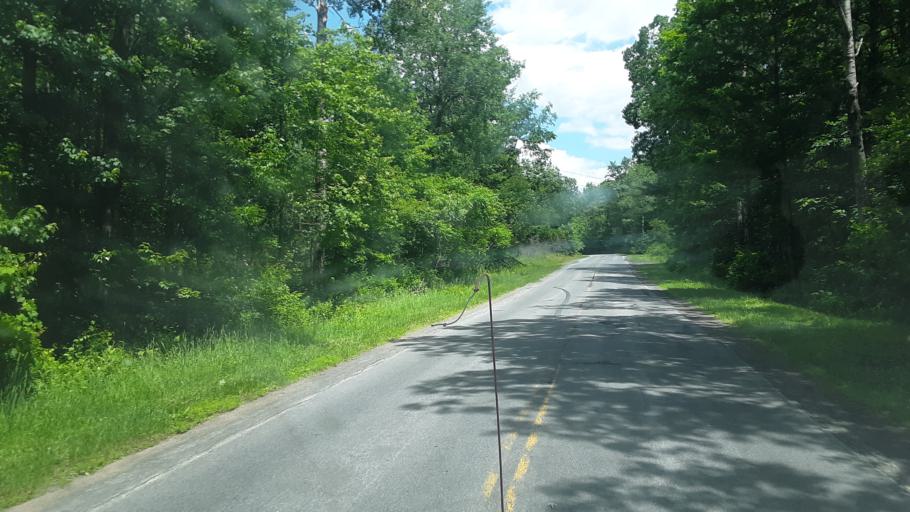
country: US
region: New York
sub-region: Oneida County
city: Rome
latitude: 43.2593
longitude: -75.5907
